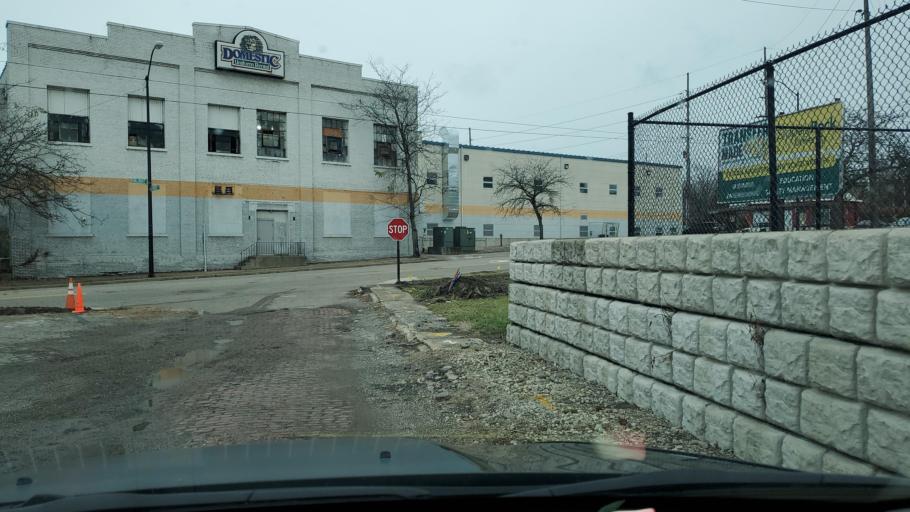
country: US
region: Ohio
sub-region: Mahoning County
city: Youngstown
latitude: 41.1058
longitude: -80.6554
